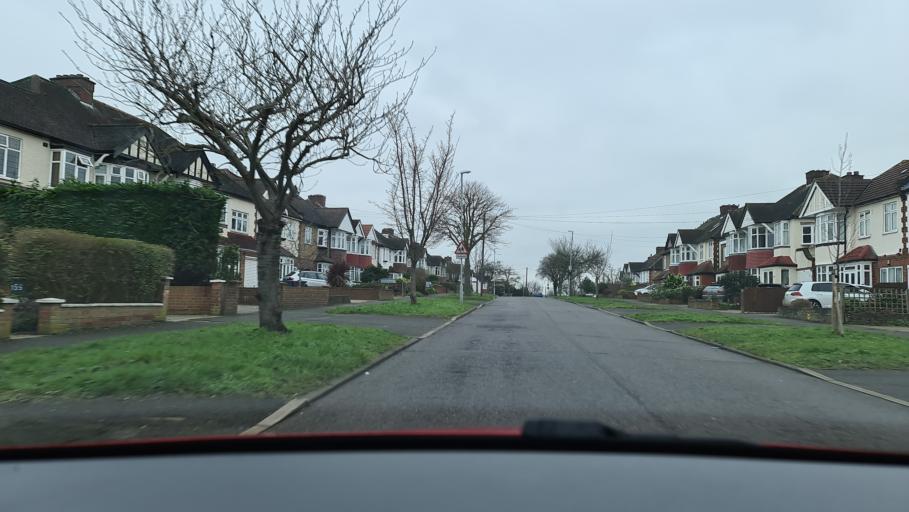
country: GB
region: England
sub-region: Greater London
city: New Malden
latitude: 51.3887
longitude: -0.2743
